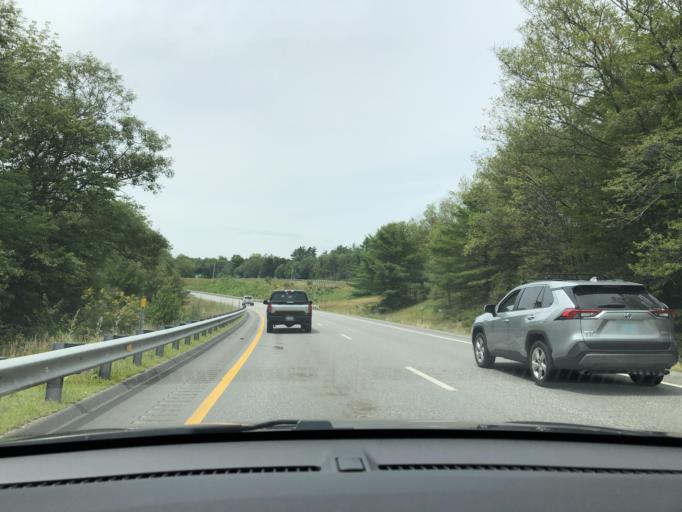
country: US
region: New Hampshire
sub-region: Merrimack County
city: Webster
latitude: 43.2732
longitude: -71.7884
